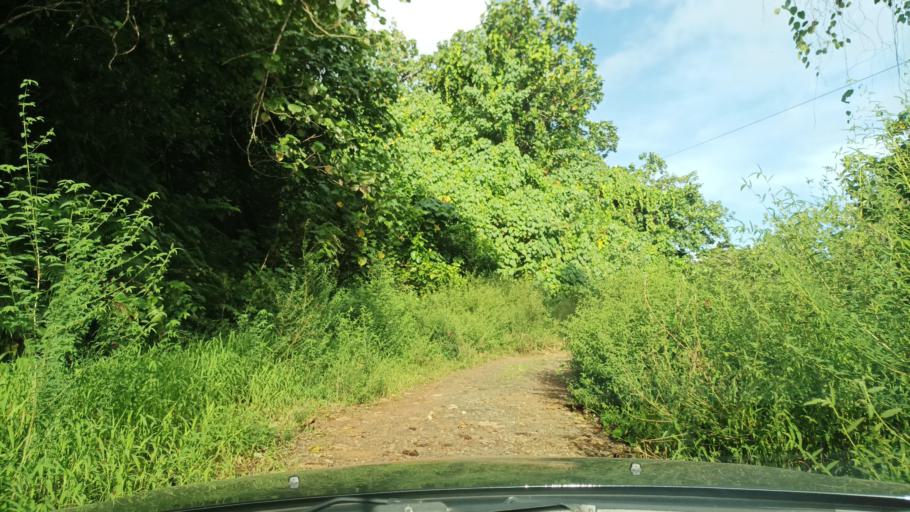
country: FM
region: Kosrae
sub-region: Utwe Municipality
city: Utwe
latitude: 5.2756
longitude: 162.9426
